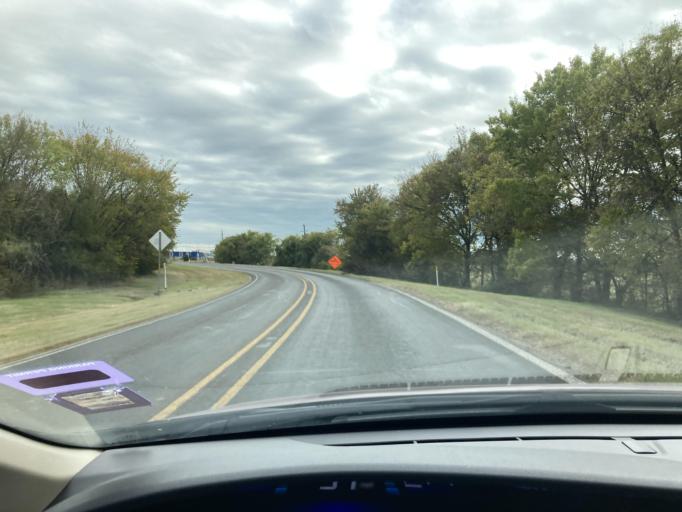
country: US
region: Texas
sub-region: Navarro County
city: Corsicana
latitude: 32.0666
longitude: -96.5020
